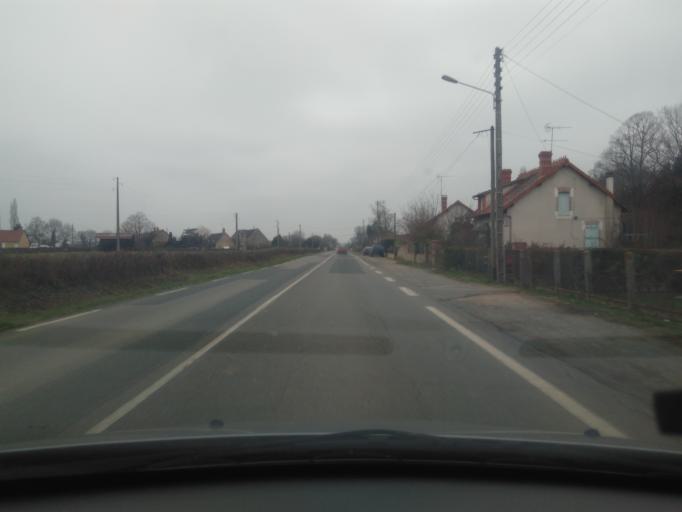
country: FR
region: Centre
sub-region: Departement du Cher
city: Charenton-du-Cher
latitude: 46.7313
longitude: 2.6247
